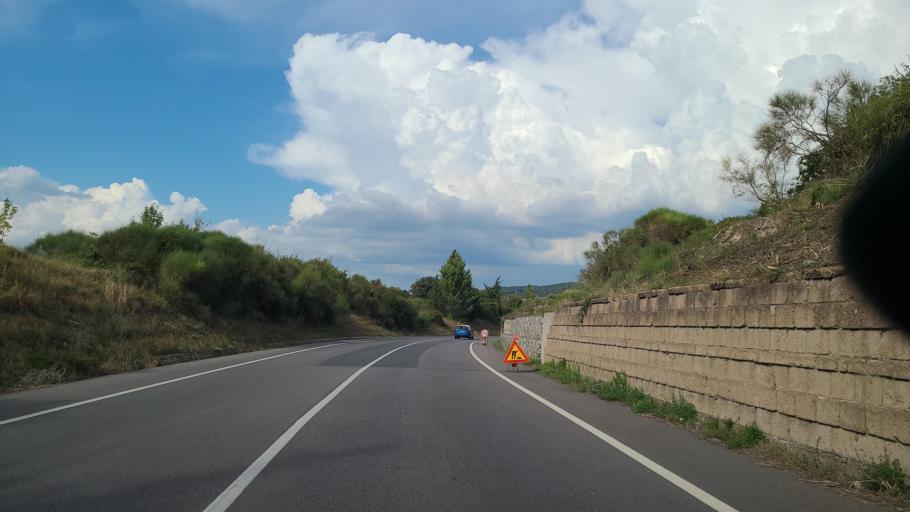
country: IT
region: Tuscany
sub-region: Province of Pisa
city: Volterra
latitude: 43.3935
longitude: 10.9550
